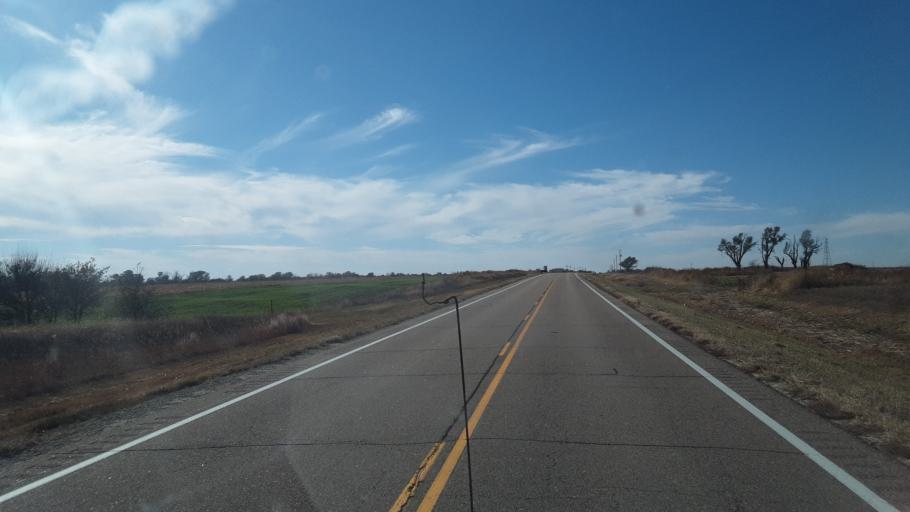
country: US
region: Kansas
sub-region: Pawnee County
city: Larned
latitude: 38.1896
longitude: -99.3057
